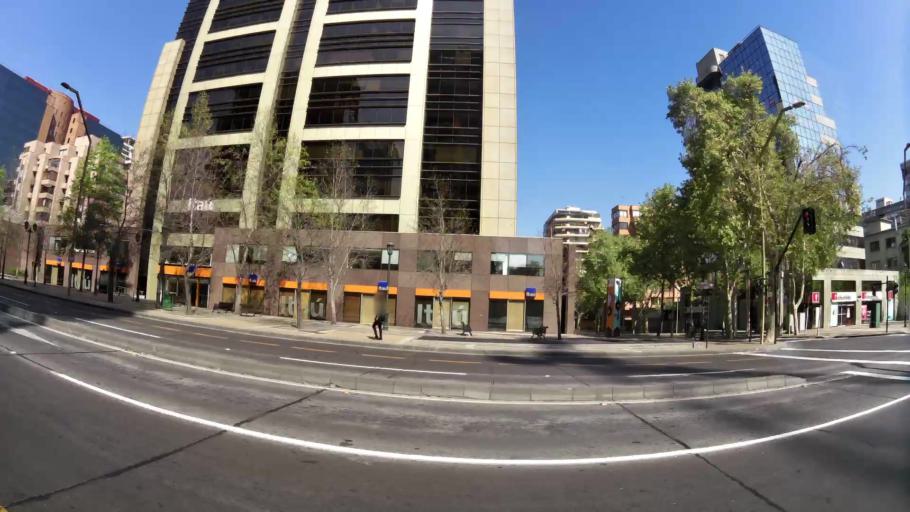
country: CL
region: Santiago Metropolitan
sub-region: Provincia de Santiago
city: Villa Presidente Frei, Nunoa, Santiago, Chile
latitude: -33.4164
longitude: -70.5939
